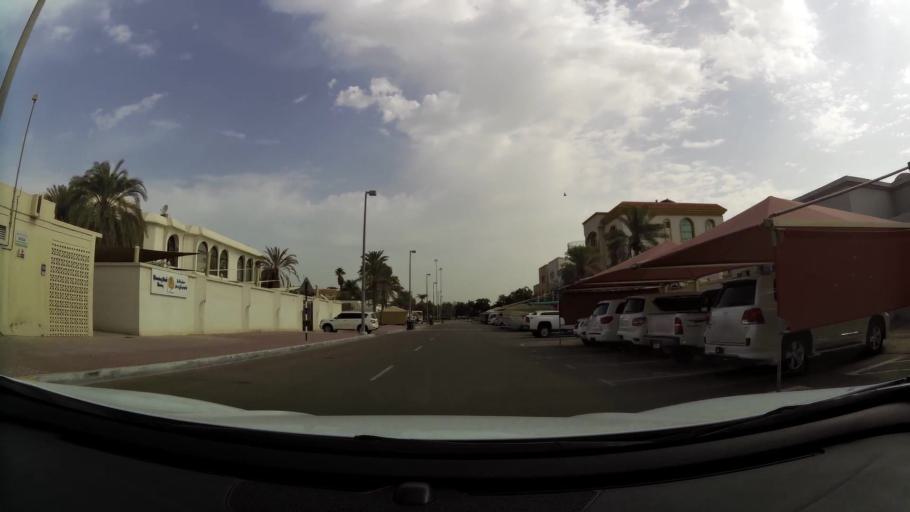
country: AE
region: Abu Dhabi
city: Abu Dhabi
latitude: 24.4342
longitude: 54.3738
